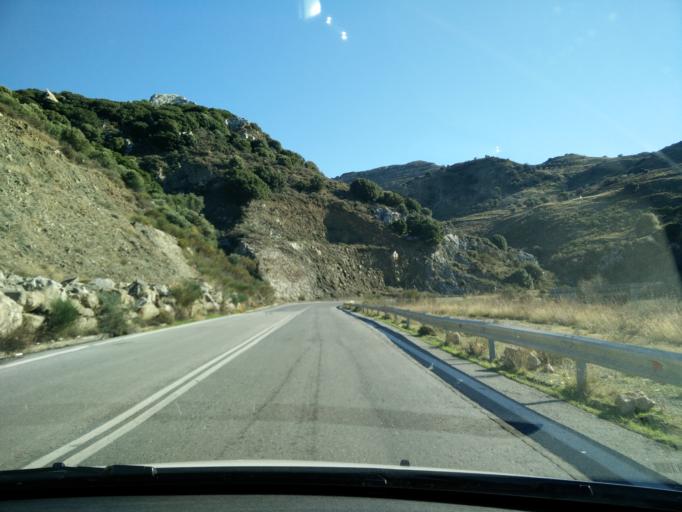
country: GR
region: Crete
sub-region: Nomos Irakleiou
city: Arkalochori
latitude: 35.0699
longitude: 25.3612
